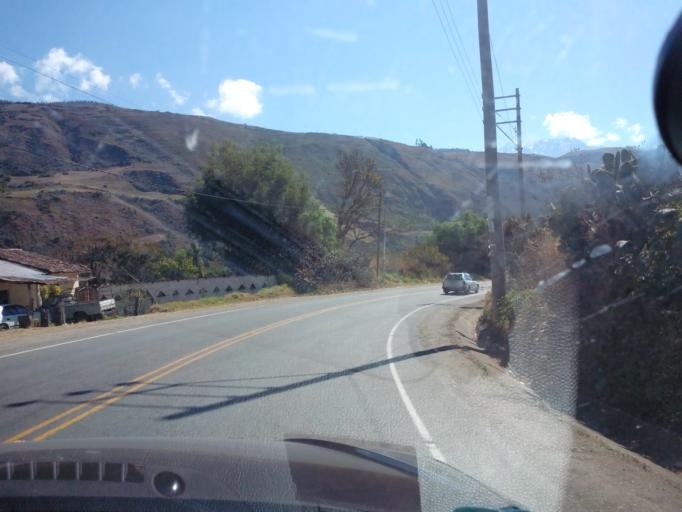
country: PE
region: Apurimac
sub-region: Provincia de Abancay
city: Curahuasi
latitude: -13.5561
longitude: -72.7388
